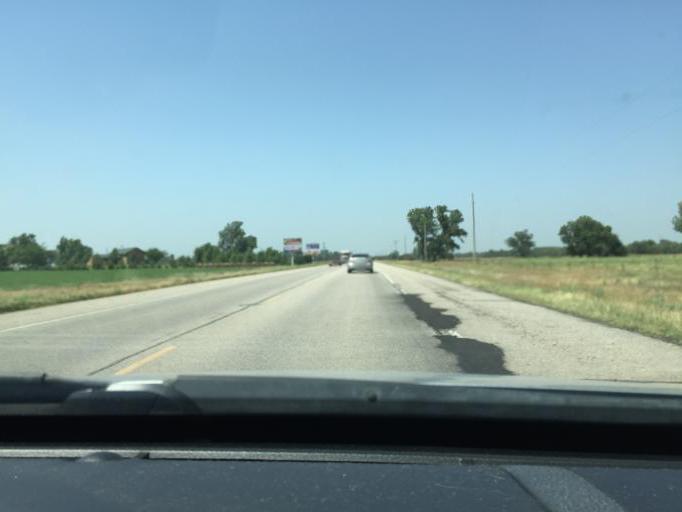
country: US
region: Kansas
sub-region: Reno County
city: South Hutchinson
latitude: 37.9915
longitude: -97.8668
